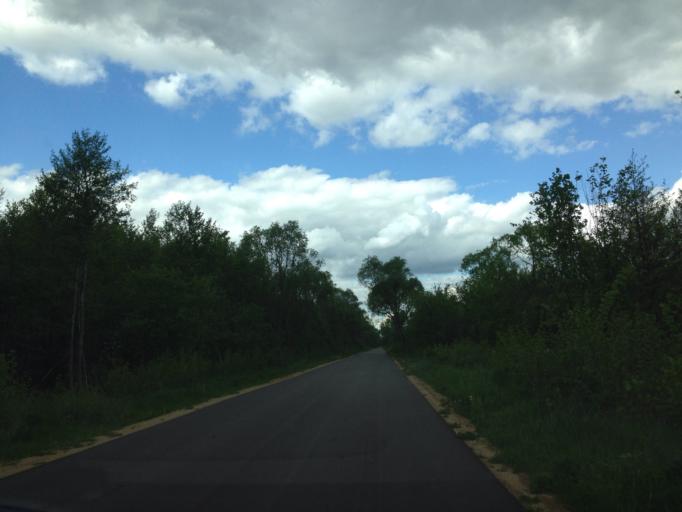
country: PL
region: Podlasie
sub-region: Powiat bialostocki
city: Tykocin
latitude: 53.3097
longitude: 22.6033
